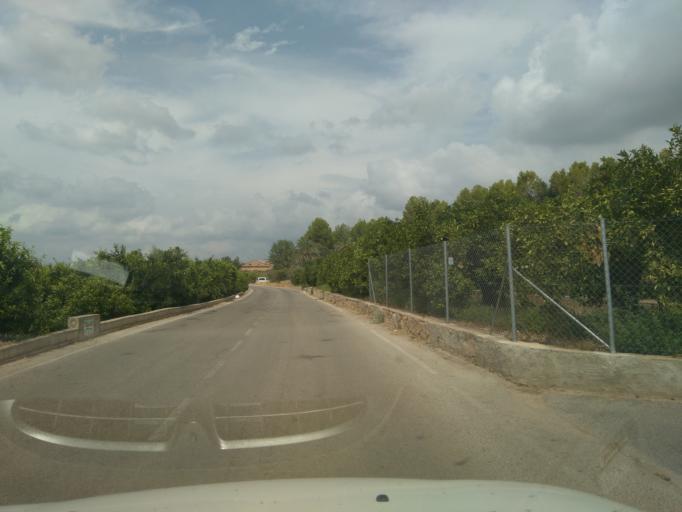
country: ES
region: Valencia
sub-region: Provincia de Valencia
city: La Pobla Llarga
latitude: 39.0859
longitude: -0.4235
